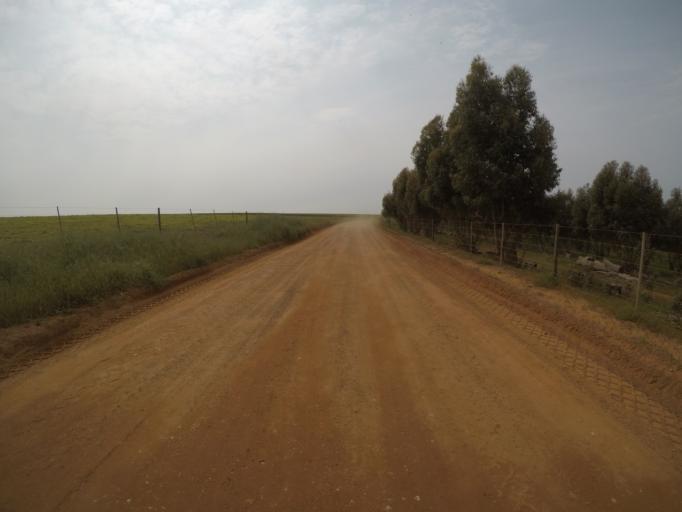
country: ZA
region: Western Cape
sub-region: City of Cape Town
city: Kraaifontein
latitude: -33.7240
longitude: 18.6552
